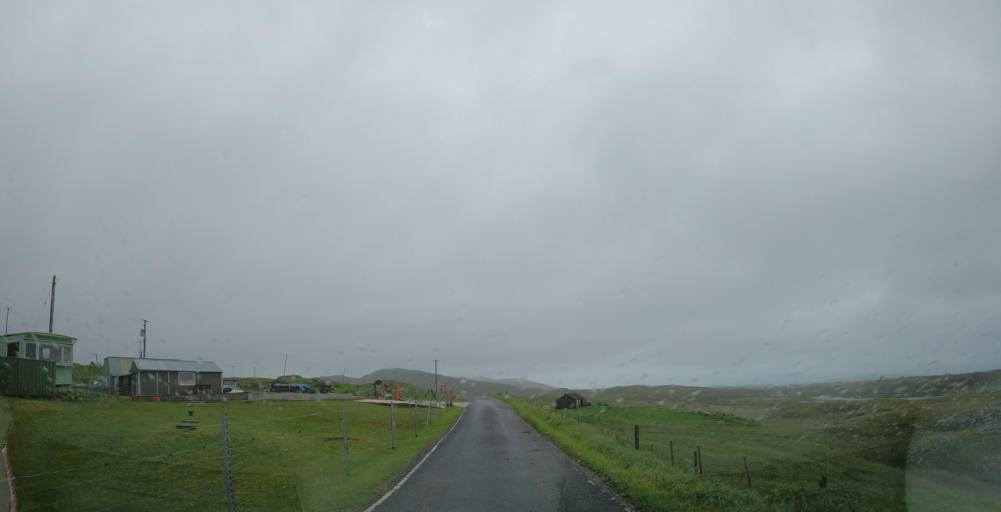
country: GB
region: Scotland
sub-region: Eilean Siar
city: Barra
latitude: 56.9864
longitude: -7.4109
